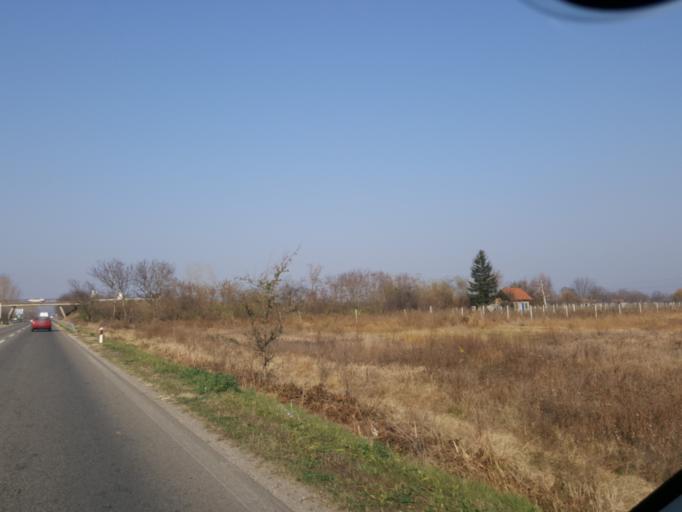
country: RS
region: Central Serbia
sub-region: Jablanicki Okrug
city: Leskovac
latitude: 43.0168
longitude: 21.9540
